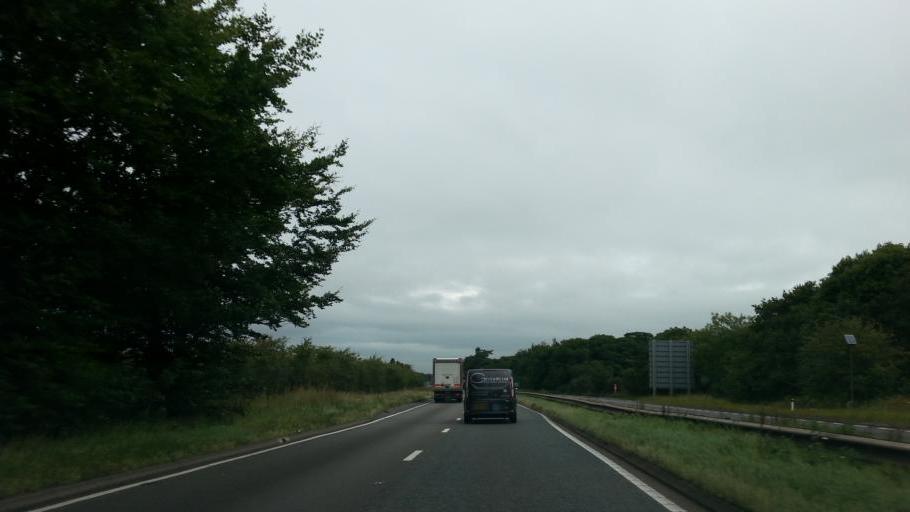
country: GB
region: England
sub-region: Nottinghamshire
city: Babworth
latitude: 53.3060
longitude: -1.0307
